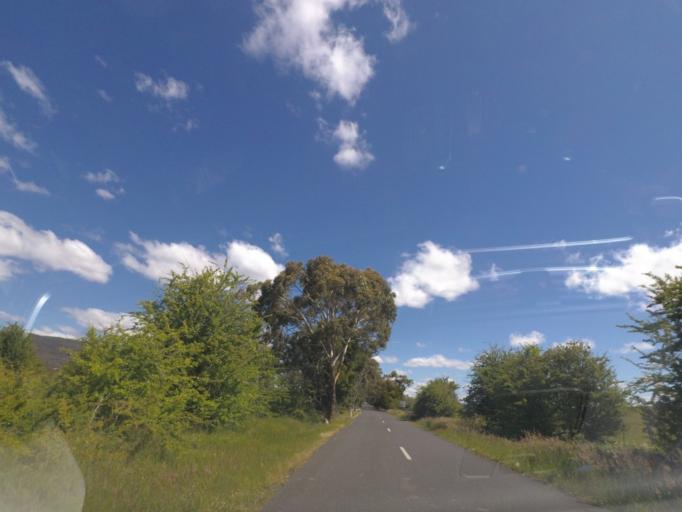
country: AU
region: Victoria
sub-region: Hume
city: Sunbury
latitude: -37.3401
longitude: 144.5573
